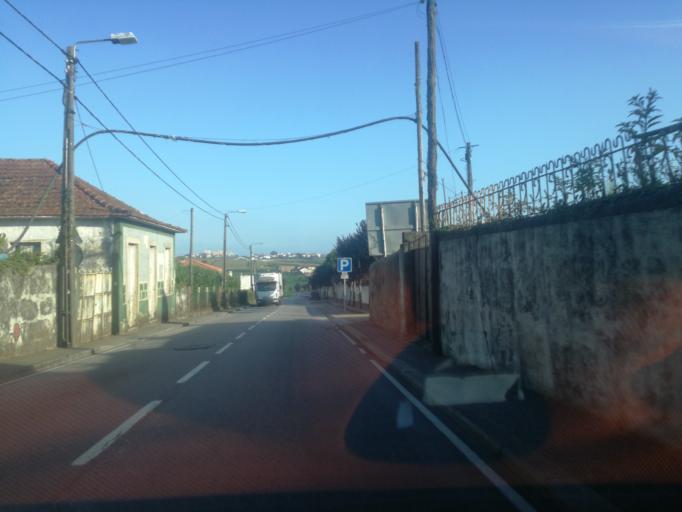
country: PT
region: Porto
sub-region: Maia
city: Gemunde
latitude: 41.2464
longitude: -8.6393
